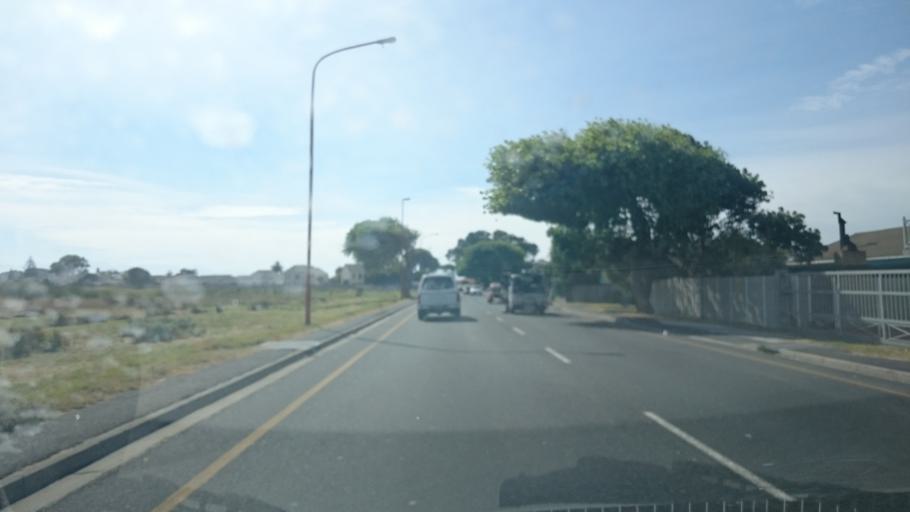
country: ZA
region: Western Cape
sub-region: City of Cape Town
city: Lansdowne
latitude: -34.0162
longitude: 18.5089
